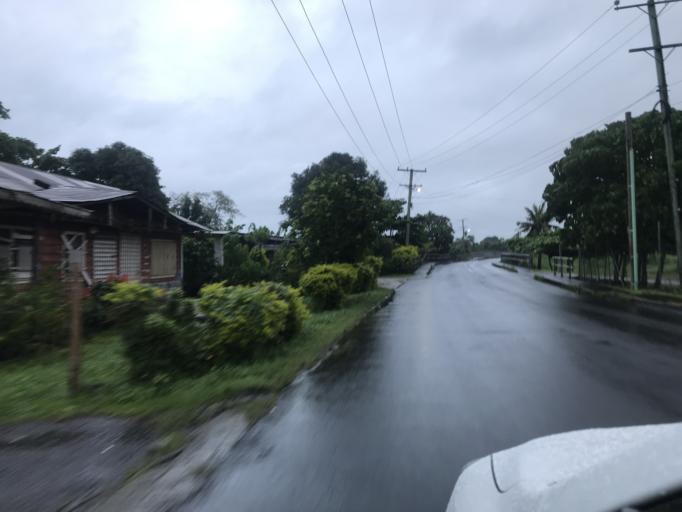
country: WS
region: Tuamasaga
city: Apia
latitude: -13.8370
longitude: -171.7606
